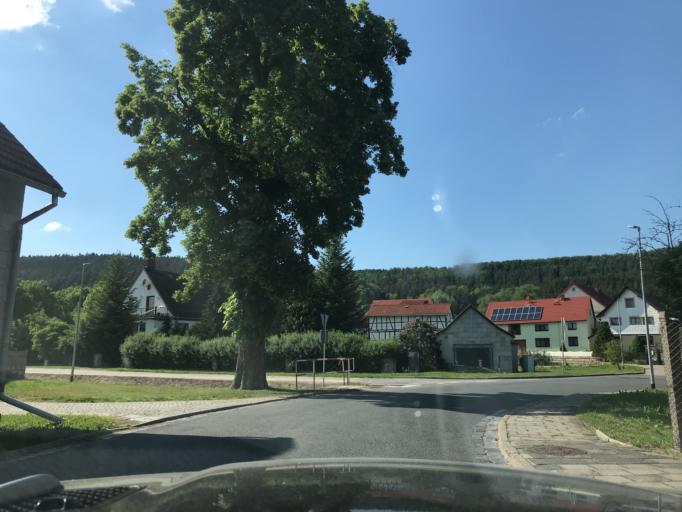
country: DE
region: Thuringia
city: Plaue
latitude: 50.7757
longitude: 10.9500
